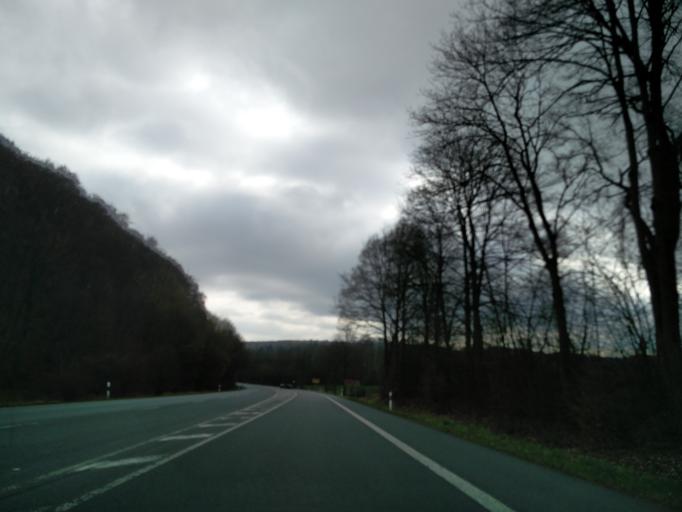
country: DE
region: North Rhine-Westphalia
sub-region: Regierungsbezirk Detmold
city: Willebadessen
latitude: 51.5456
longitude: 9.0113
